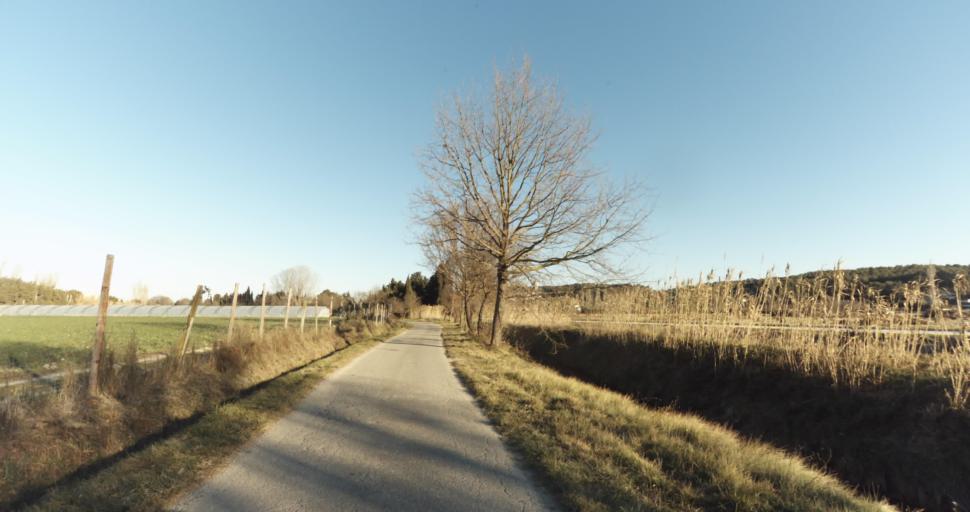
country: FR
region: Provence-Alpes-Cote d'Azur
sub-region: Departement des Bouches-du-Rhone
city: Barbentane
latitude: 43.9018
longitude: 4.7345
